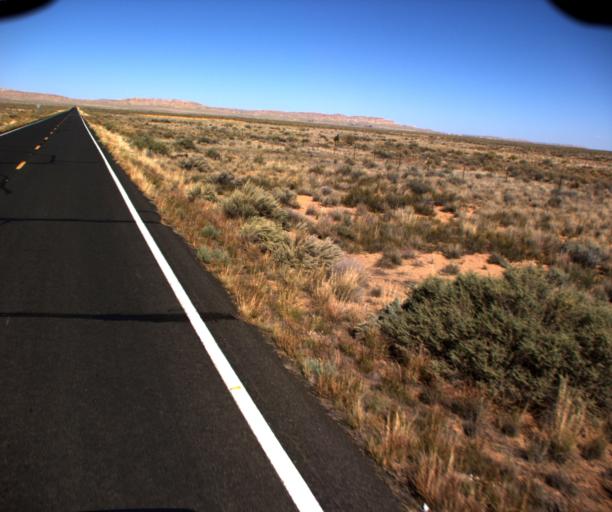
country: US
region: Arizona
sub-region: Navajo County
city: First Mesa
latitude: 35.7099
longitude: -110.5110
